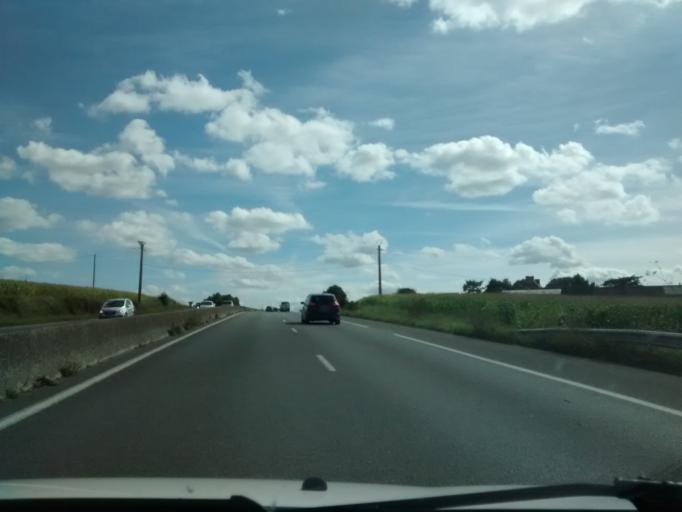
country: FR
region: Brittany
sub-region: Departement d'Ille-et-Vilaine
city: Saint-Jouan-des-Guerets
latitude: 48.5888
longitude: -1.9559
